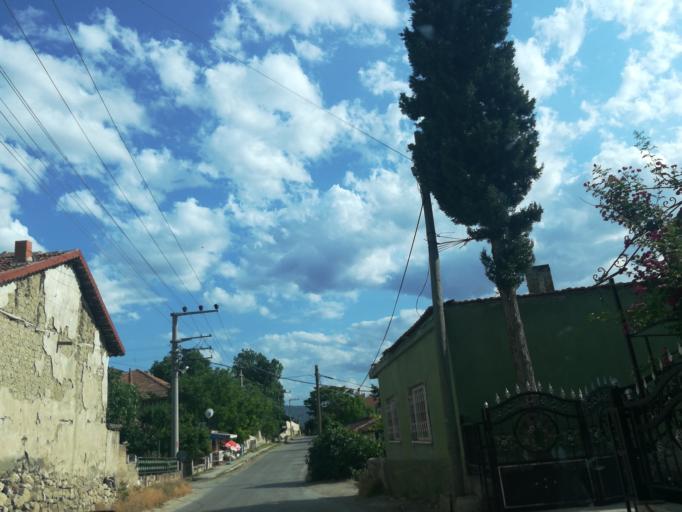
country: TR
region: Afyonkarahisar
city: Dinar
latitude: 38.0740
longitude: 30.1690
